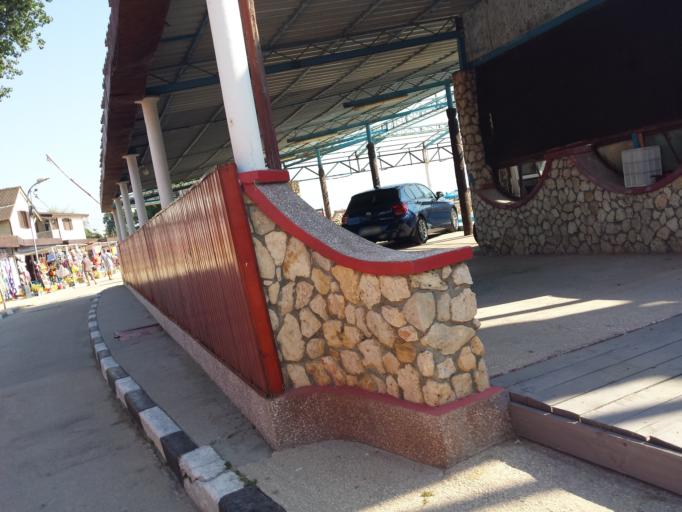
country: RO
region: Constanta
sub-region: Comuna Douazeci si Trei August
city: Douazeci si Trei August
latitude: 43.8590
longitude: 28.6060
